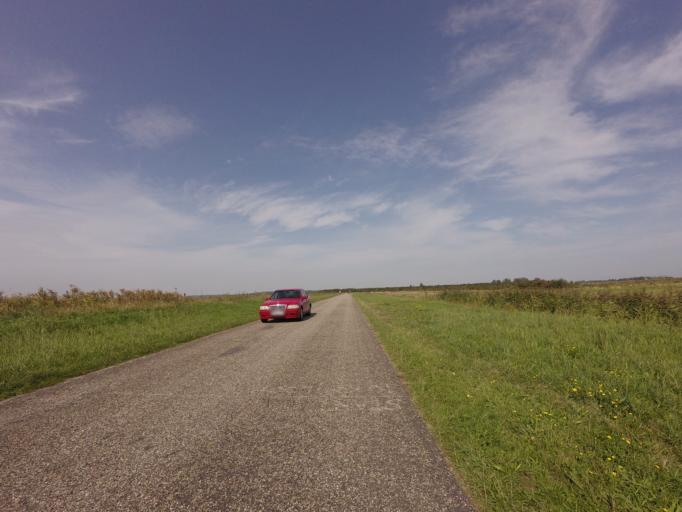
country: NL
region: Groningen
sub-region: Gemeente De Marne
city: Ulrum
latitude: 53.3508
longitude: 6.2662
